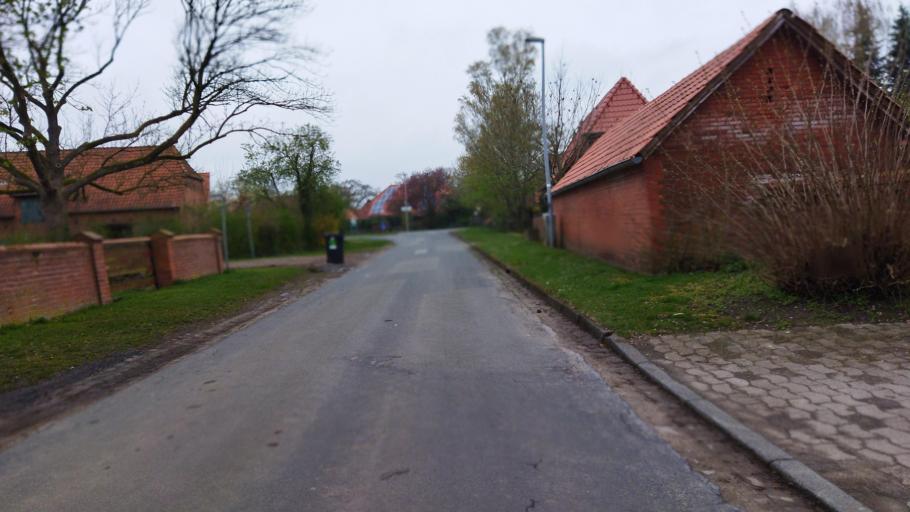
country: DE
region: Lower Saxony
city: Schweringen
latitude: 52.7474
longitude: 9.1853
